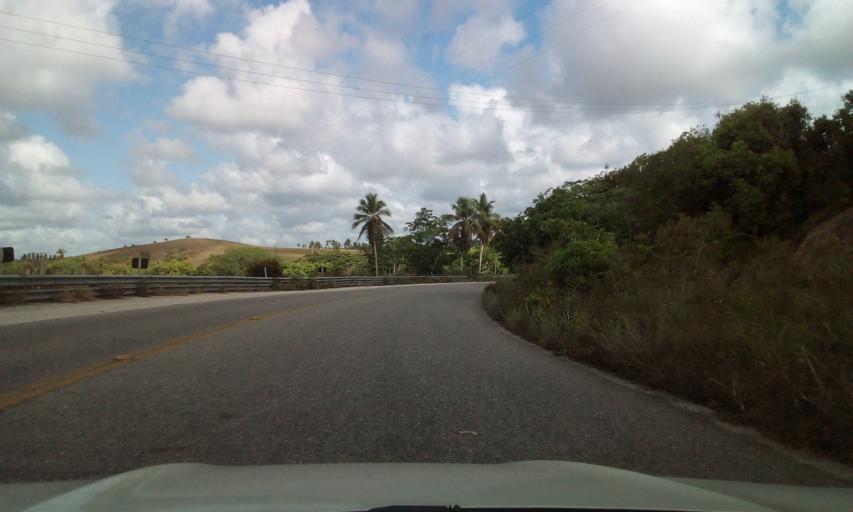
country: BR
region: Sergipe
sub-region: Indiaroba
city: Indiaroba
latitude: -11.4763
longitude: -37.4915
